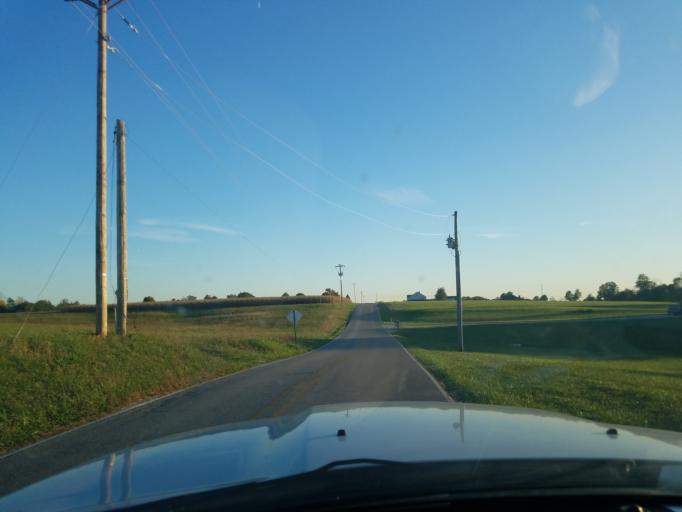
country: US
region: Indiana
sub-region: Floyd County
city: Galena
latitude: 38.4143
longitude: -85.9110
